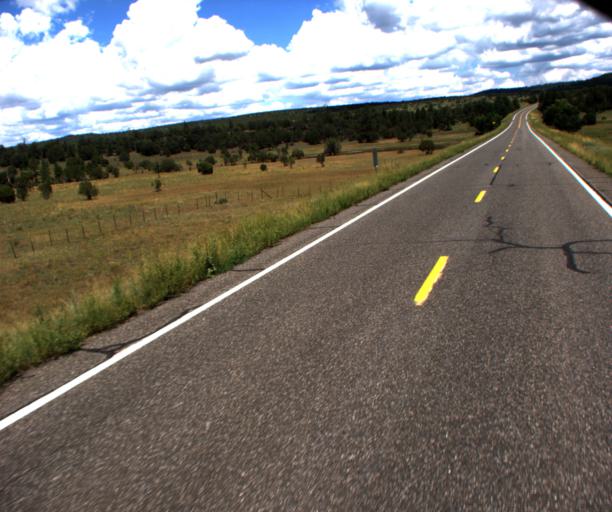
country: US
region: Arizona
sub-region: Gila County
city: Pine
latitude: 34.5014
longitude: -111.5797
